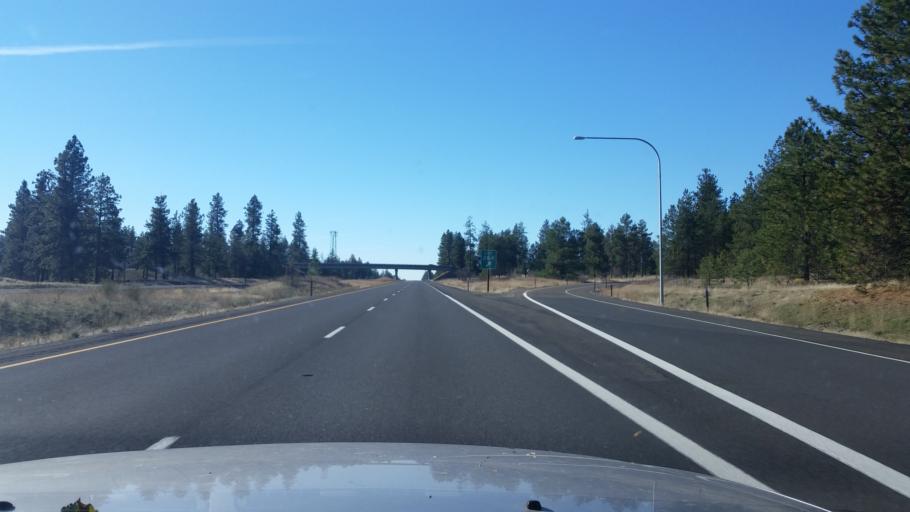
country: US
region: Washington
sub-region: Spokane County
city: Medical Lake
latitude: 47.5067
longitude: -117.6879
